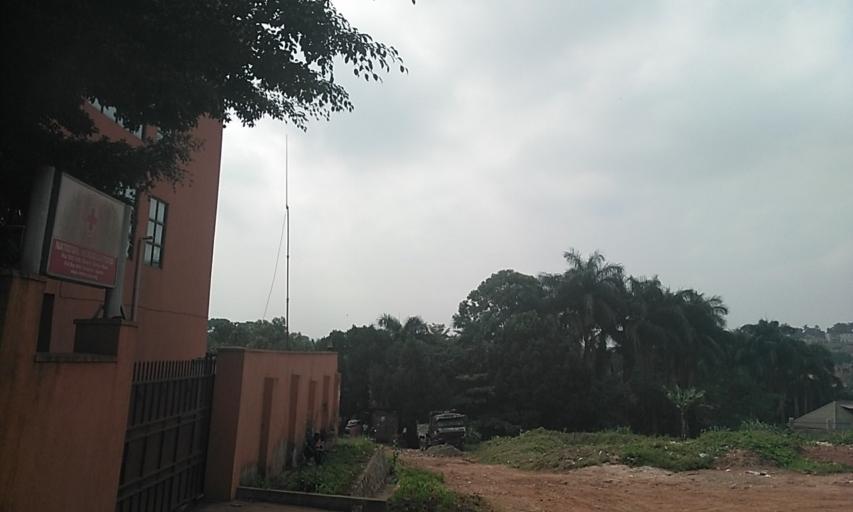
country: UG
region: Central Region
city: Kampala Central Division
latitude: 0.3054
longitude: 32.5602
